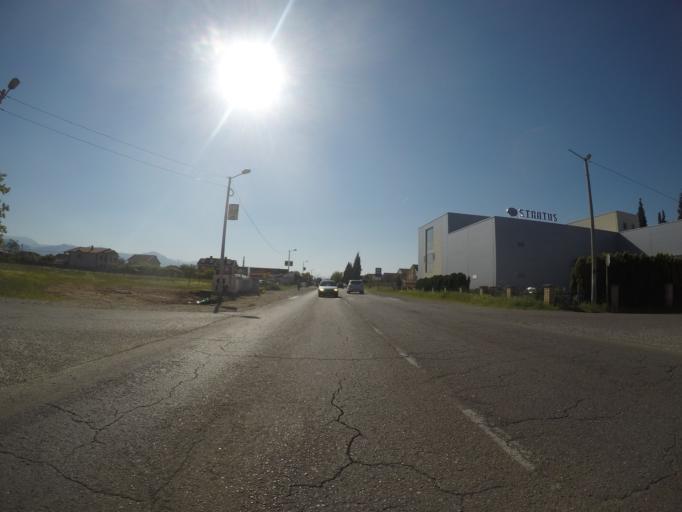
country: ME
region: Podgorica
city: Podgorica
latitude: 42.4418
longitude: 19.2164
